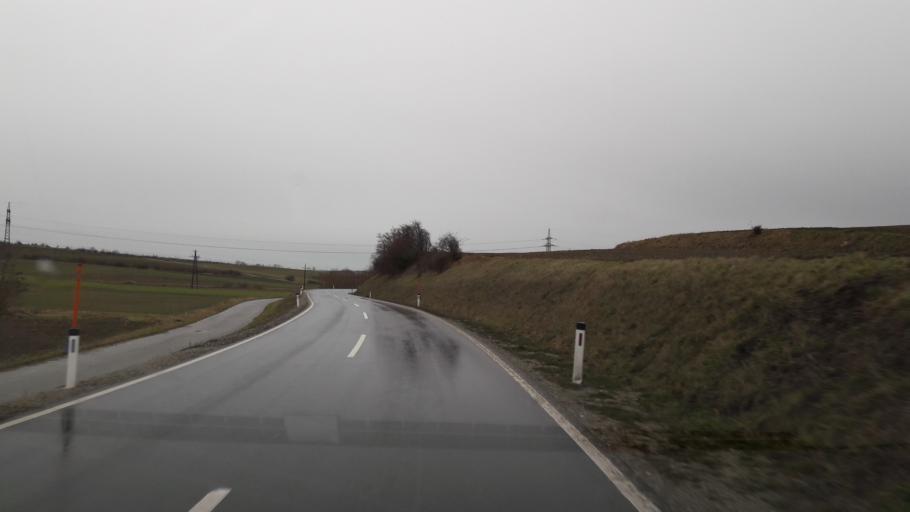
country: AT
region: Lower Austria
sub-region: Politischer Bezirk Mistelbach
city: Hochleithen
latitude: 48.4331
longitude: 16.5461
